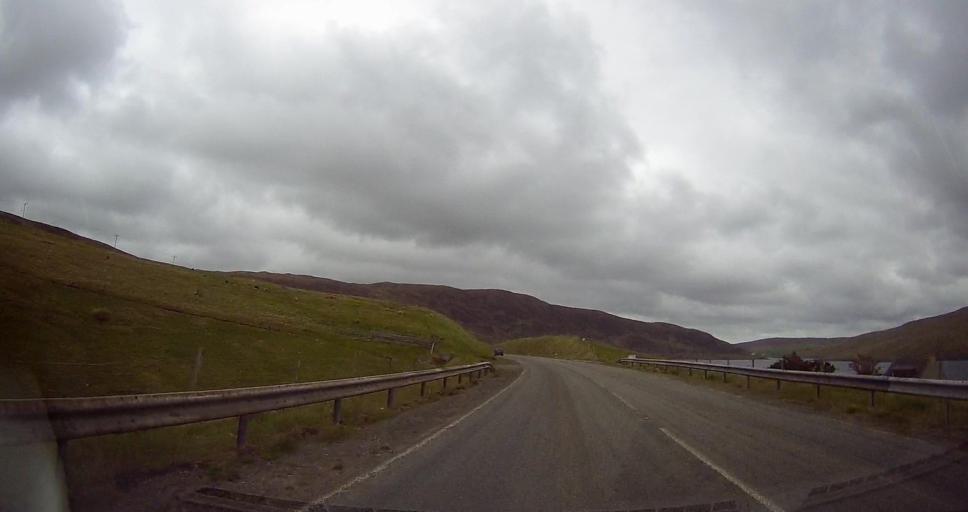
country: GB
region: Scotland
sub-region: Shetland Islands
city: Lerwick
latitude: 60.3712
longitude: -1.3155
